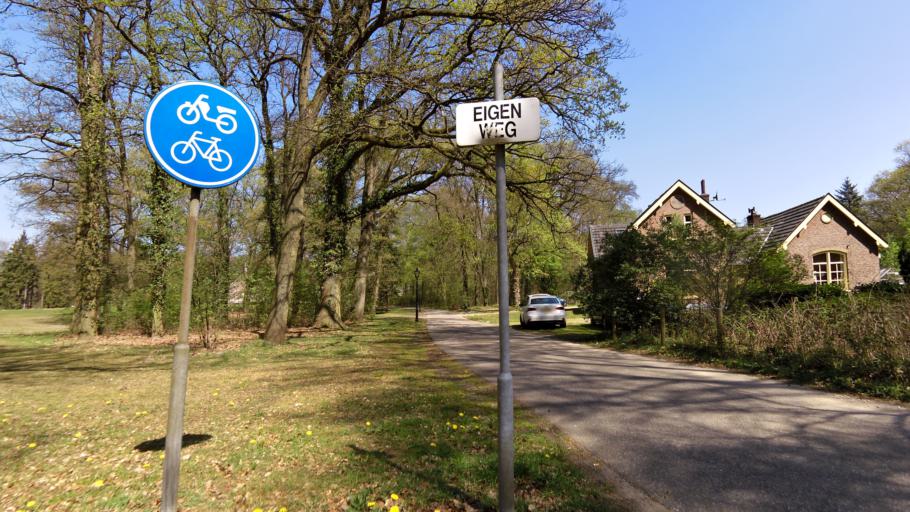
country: NL
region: Gelderland
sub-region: Gemeente Arnhem
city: Hoogkamp
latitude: 52.0274
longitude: 5.8717
